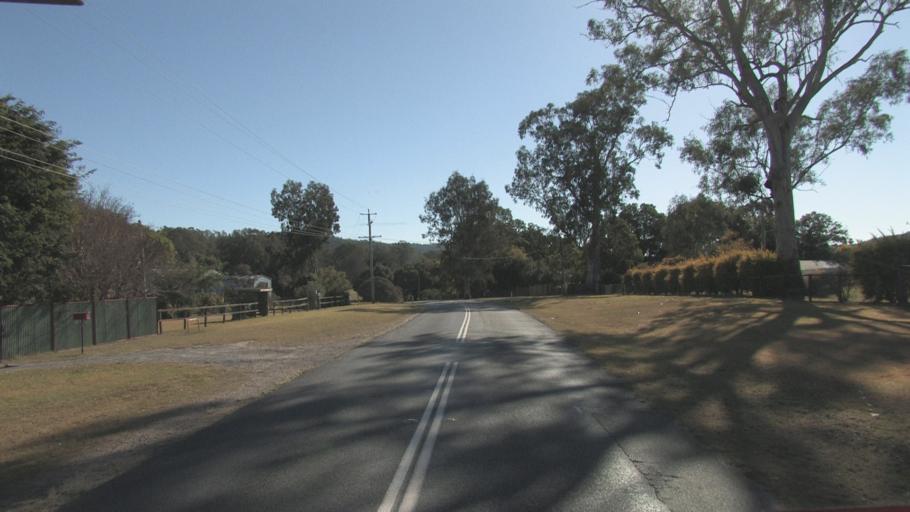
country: AU
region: Queensland
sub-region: Logan
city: Windaroo
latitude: -27.8101
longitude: 153.1707
